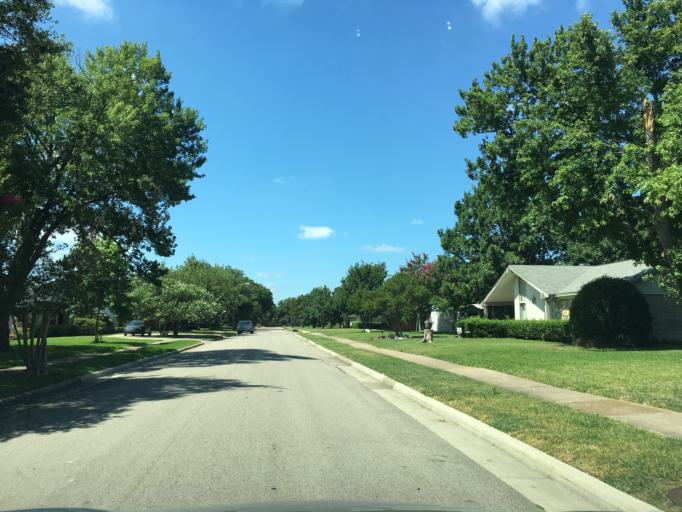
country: US
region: Texas
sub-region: Dallas County
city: Garland
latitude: 32.8501
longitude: -96.6498
